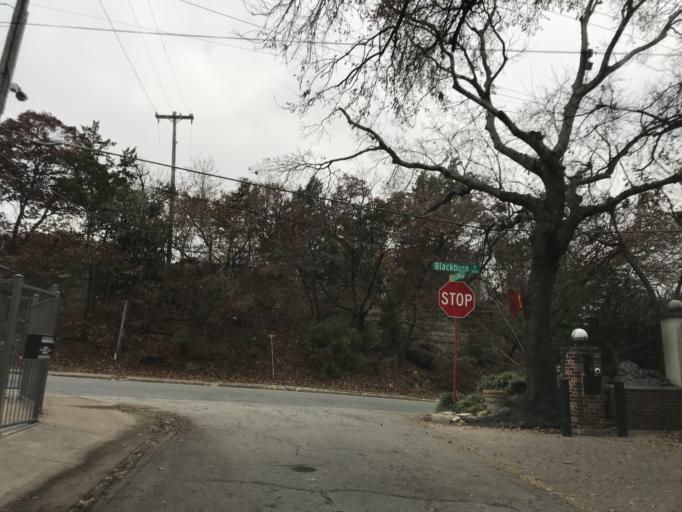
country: US
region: Texas
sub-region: Dallas County
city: Highland Park
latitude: 32.8122
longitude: -96.7994
